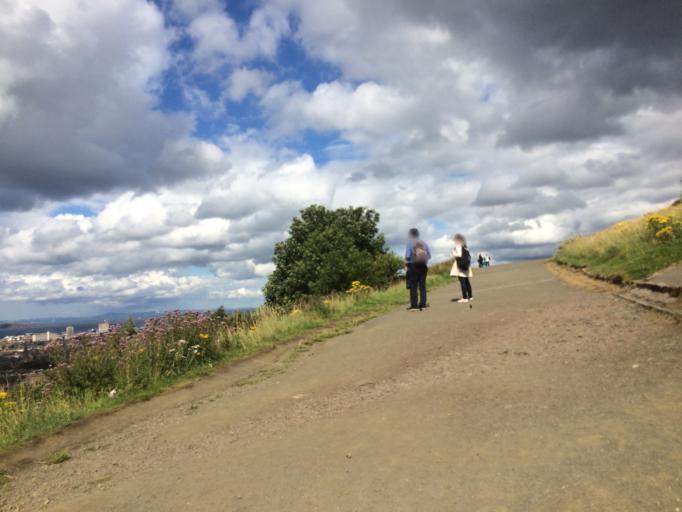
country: GB
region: Scotland
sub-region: Edinburgh
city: Edinburgh
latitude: 55.9558
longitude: -3.1834
